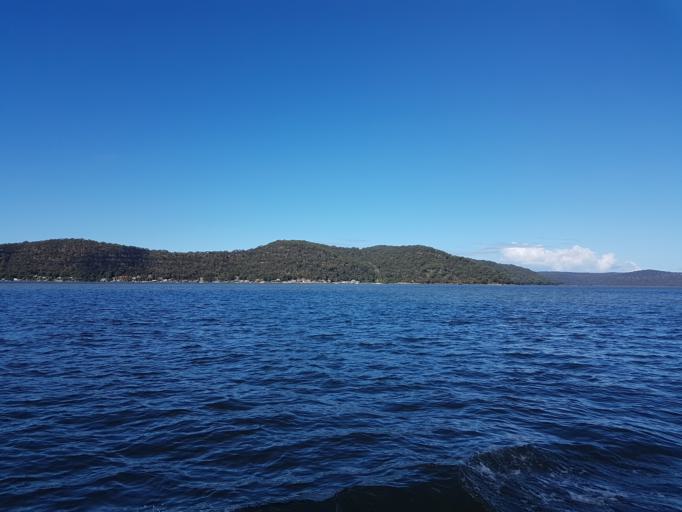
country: AU
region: New South Wales
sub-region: Gosford Shire
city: Umina
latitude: -33.5446
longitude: 151.2327
